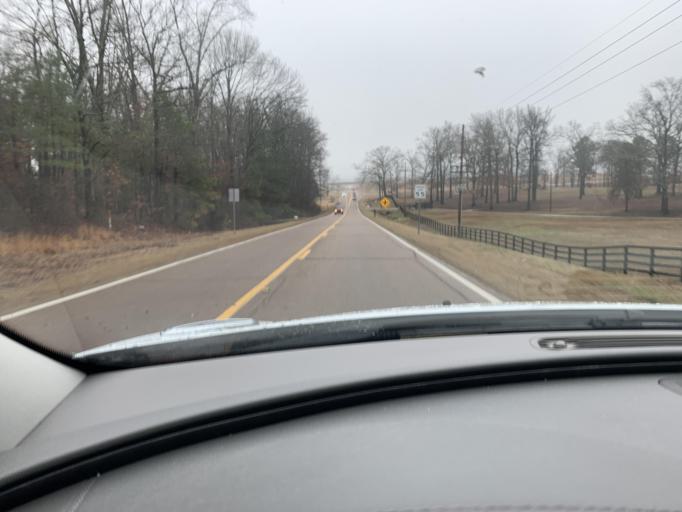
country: US
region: Mississippi
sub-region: De Soto County
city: Hernando
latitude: 34.8557
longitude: -89.9952
